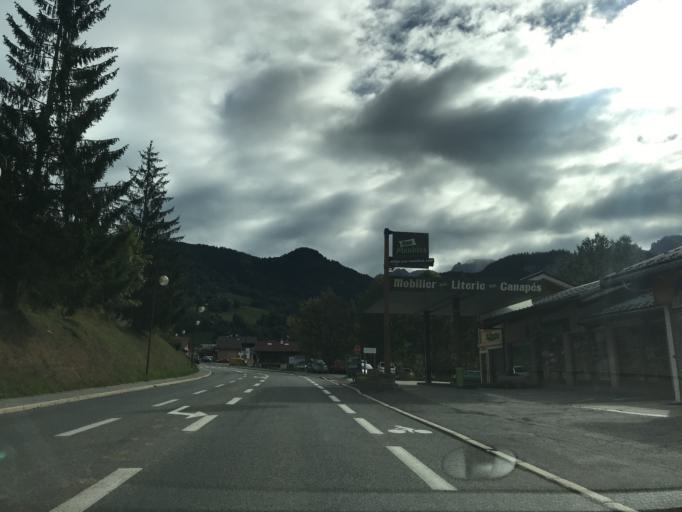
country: FR
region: Rhone-Alpes
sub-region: Departement de la Haute-Savoie
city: Saint-Jean-de-Sixt
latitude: 45.9213
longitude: 6.4025
